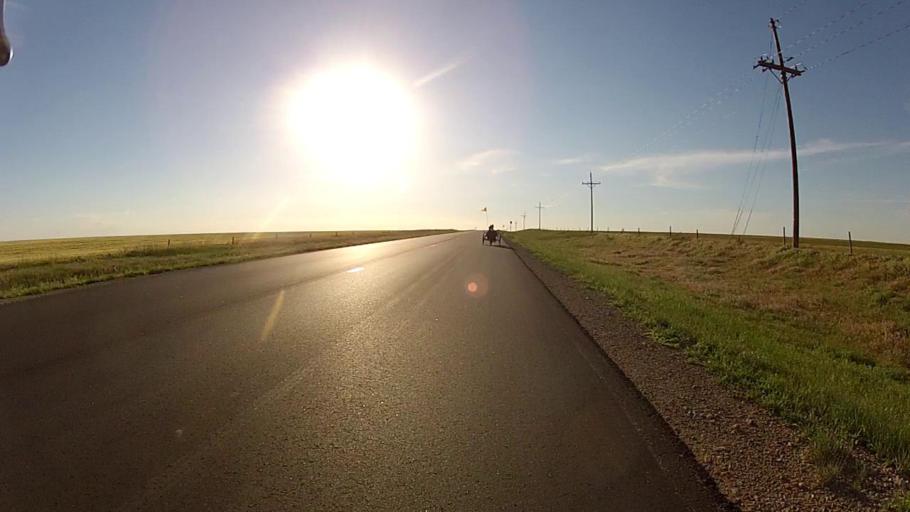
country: US
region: Kansas
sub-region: Comanche County
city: Coldwater
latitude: 37.2816
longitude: -99.1639
